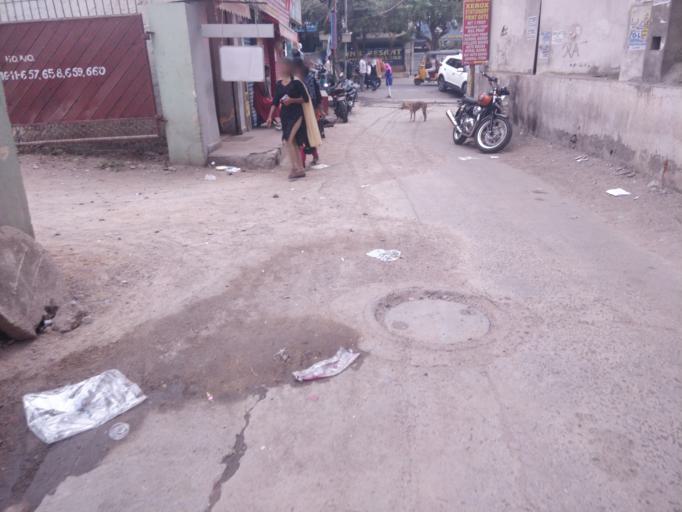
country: IN
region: Telangana
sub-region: Rangareddi
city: Gaddi Annaram
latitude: 17.3672
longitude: 78.5218
